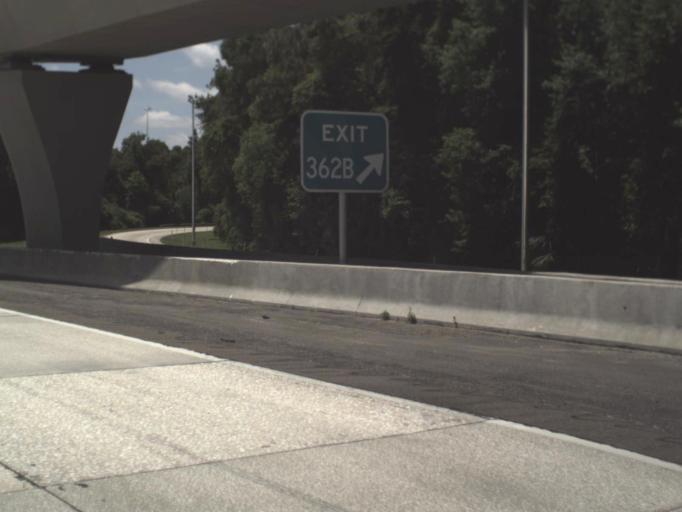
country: US
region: Florida
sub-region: Duval County
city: Jacksonville
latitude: 30.4625
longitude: -81.6488
